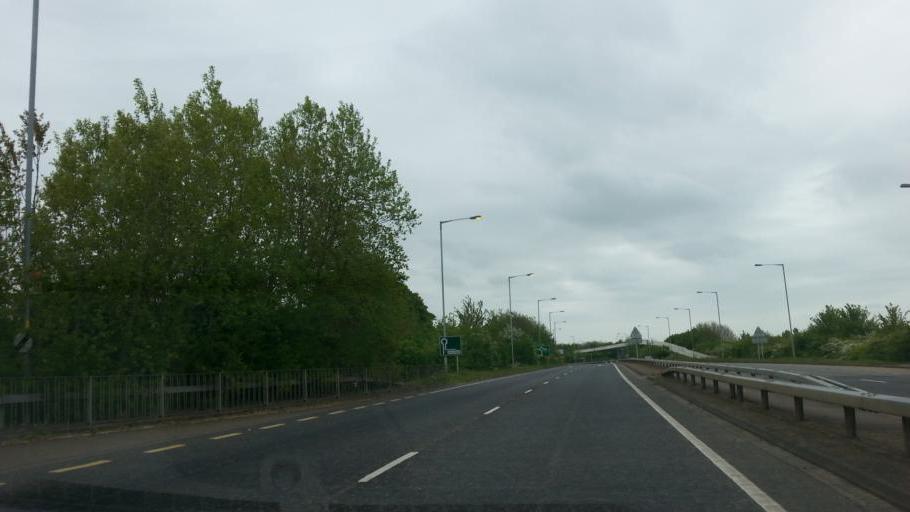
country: GB
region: England
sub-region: Peterborough
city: Glinton
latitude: 52.6295
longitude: -0.2957
